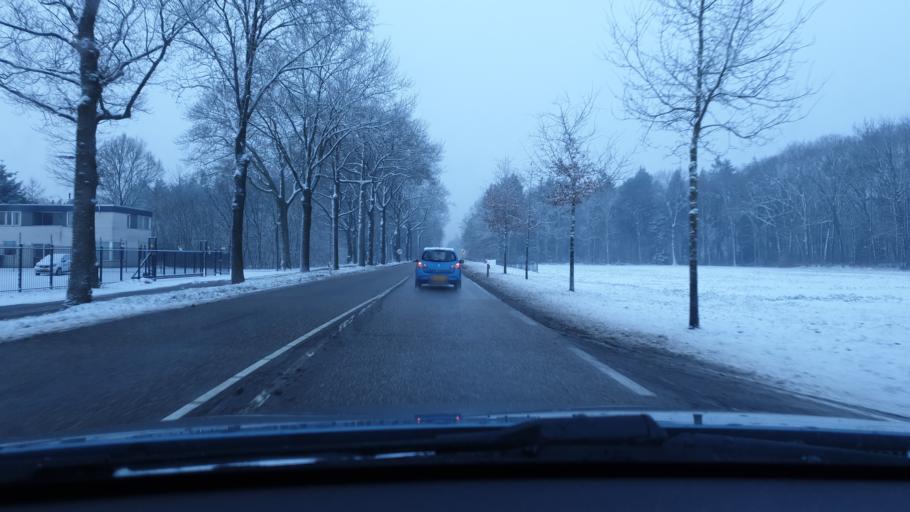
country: NL
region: North Brabant
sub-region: Gemeente Landerd
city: Zeeland
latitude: 51.6865
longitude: 5.6590
